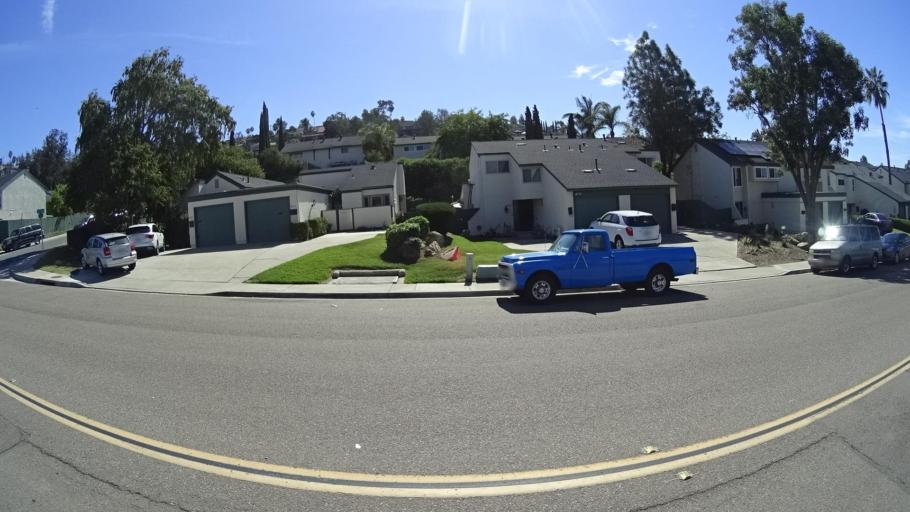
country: US
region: California
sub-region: San Diego County
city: Spring Valley
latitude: 32.7276
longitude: -117.0070
